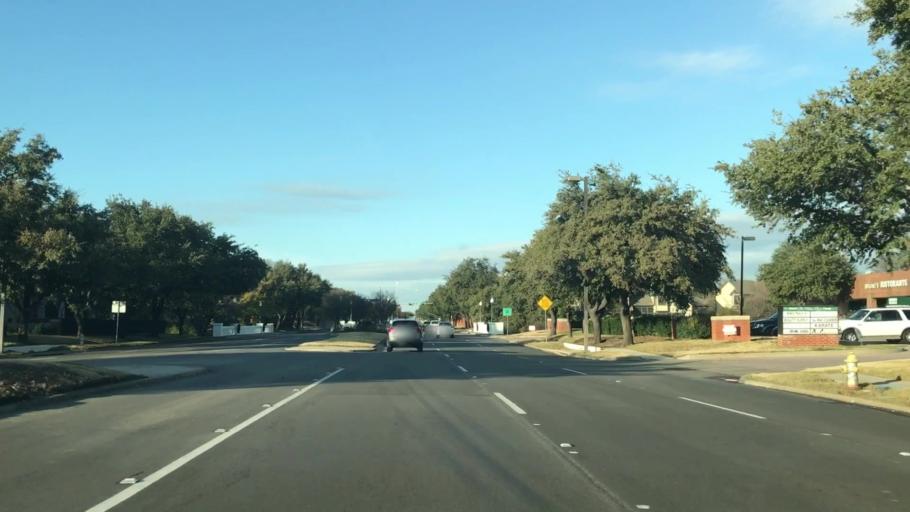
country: US
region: Texas
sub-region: Dallas County
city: Farmers Branch
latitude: 32.9340
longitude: -96.9521
